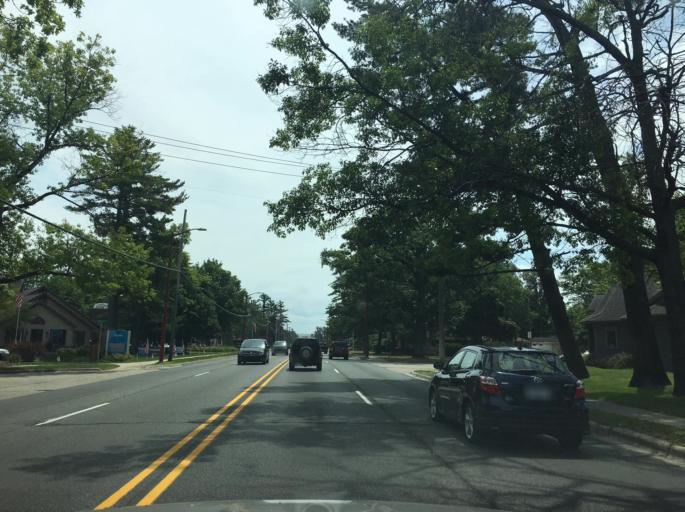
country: US
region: Michigan
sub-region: Grand Traverse County
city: Traverse City
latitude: 44.7617
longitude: -85.5843
